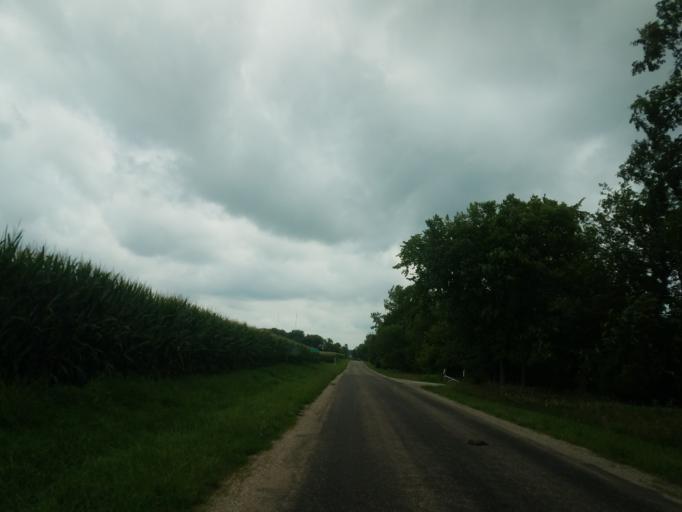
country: US
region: Illinois
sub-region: McLean County
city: Twin Grove
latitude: 40.4619
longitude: -89.0430
